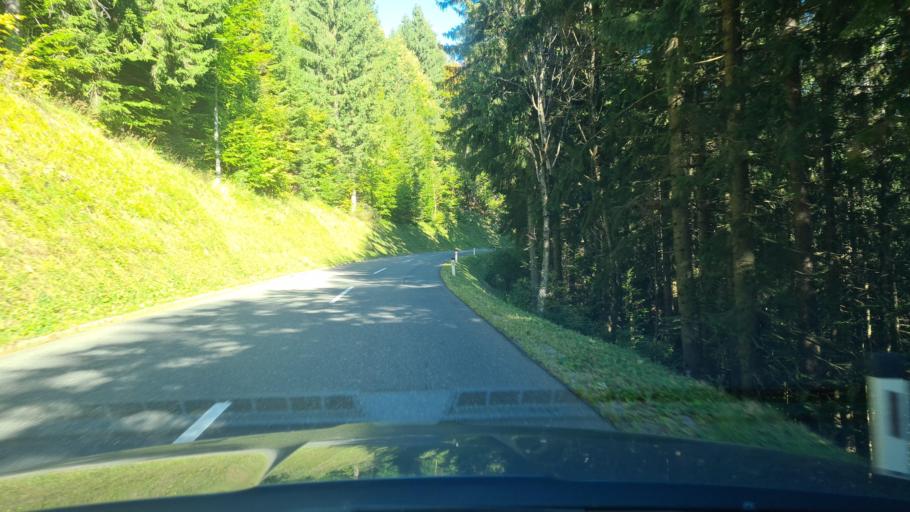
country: AT
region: Styria
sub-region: Politischer Bezirk Weiz
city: Passail
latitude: 47.3118
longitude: 15.4820
